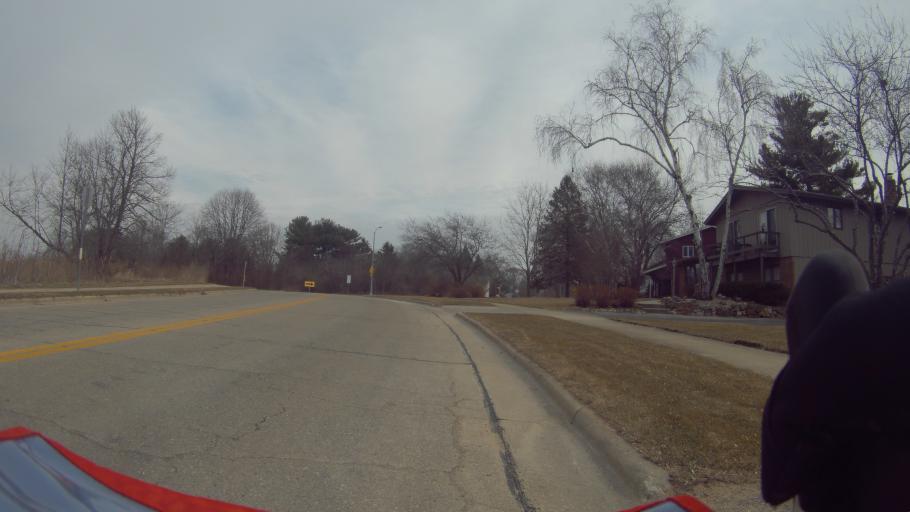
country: US
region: Wisconsin
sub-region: Dane County
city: Maple Bluff
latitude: 43.1242
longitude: -89.3729
